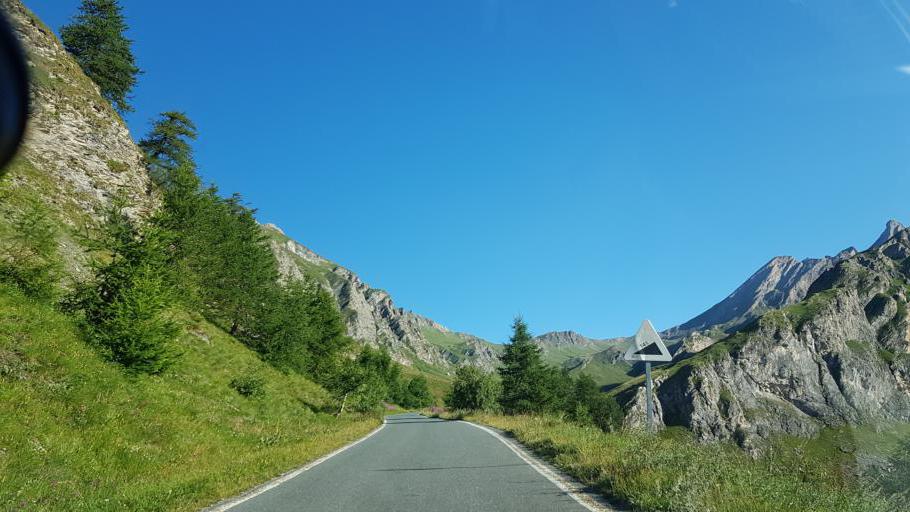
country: IT
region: Piedmont
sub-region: Provincia di Cuneo
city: Pontechianale
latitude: 44.6569
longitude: 6.9868
